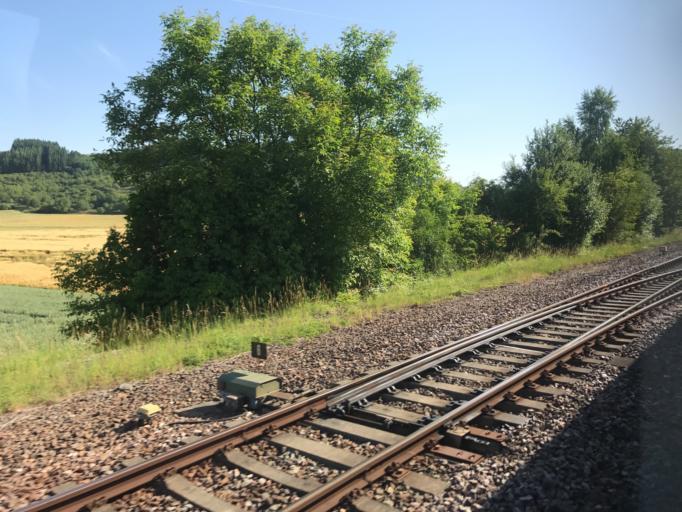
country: DE
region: Rheinland-Pfalz
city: Staudernheim
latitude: 49.7820
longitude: 7.7002
